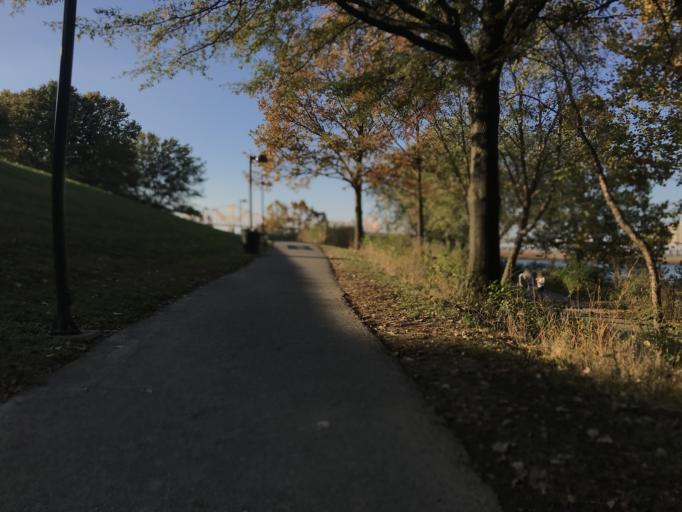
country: US
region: Kentucky
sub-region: Jefferson County
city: Louisville
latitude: 38.2605
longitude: -85.7440
